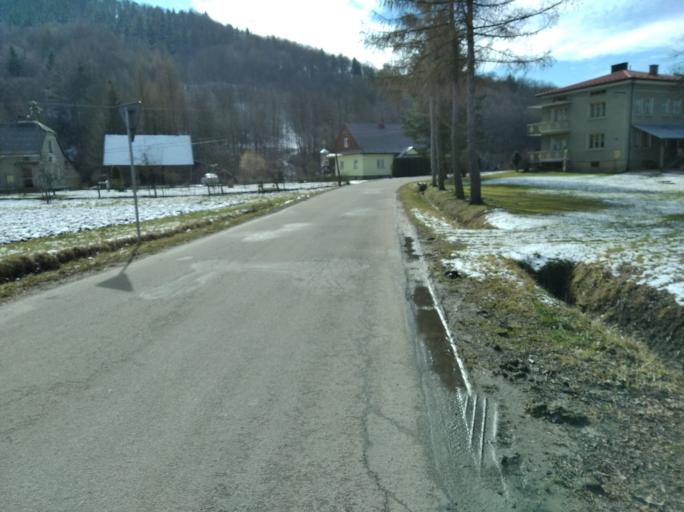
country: PL
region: Subcarpathian Voivodeship
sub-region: Powiat brzozowski
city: Jasienica Rosielna
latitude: 49.7533
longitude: 21.8852
